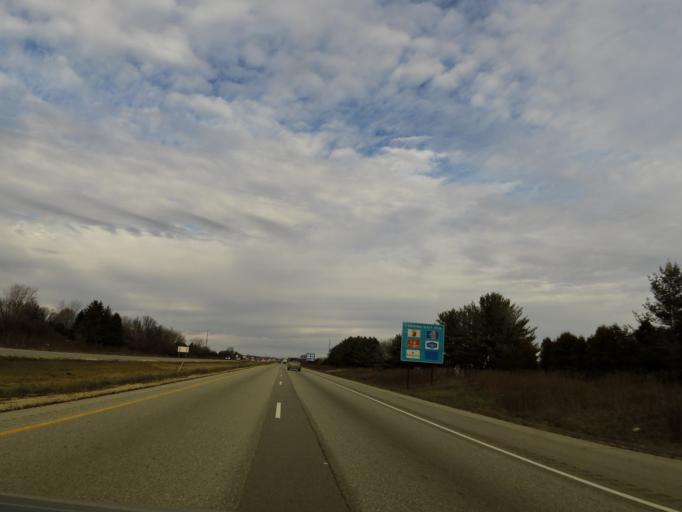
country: US
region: Wisconsin
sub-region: Rock County
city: Janesville
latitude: 42.7043
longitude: -88.9839
